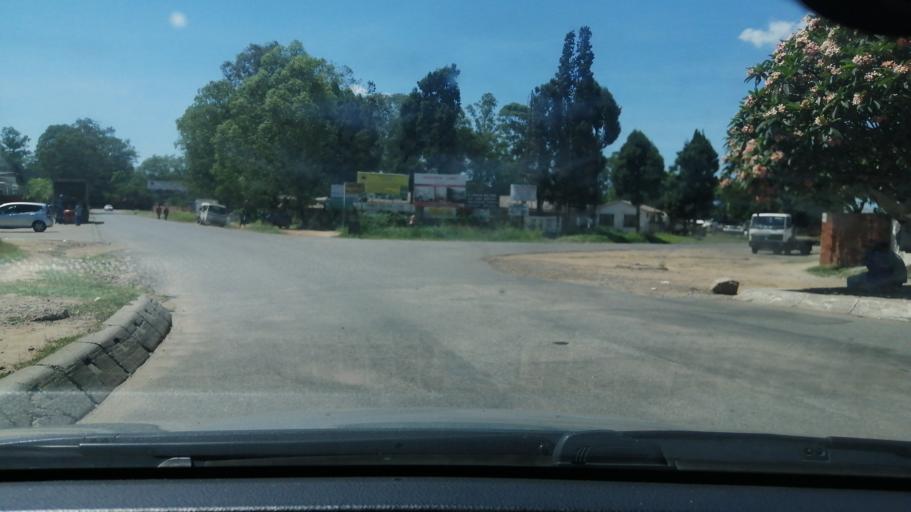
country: ZW
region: Harare
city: Epworth
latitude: -17.8397
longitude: 31.1196
